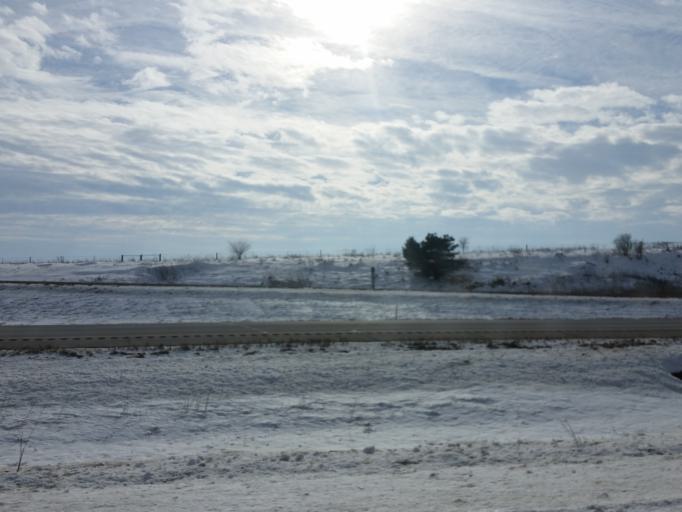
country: US
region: Iowa
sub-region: Buchanan County
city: Independence
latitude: 42.4618
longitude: -91.7568
